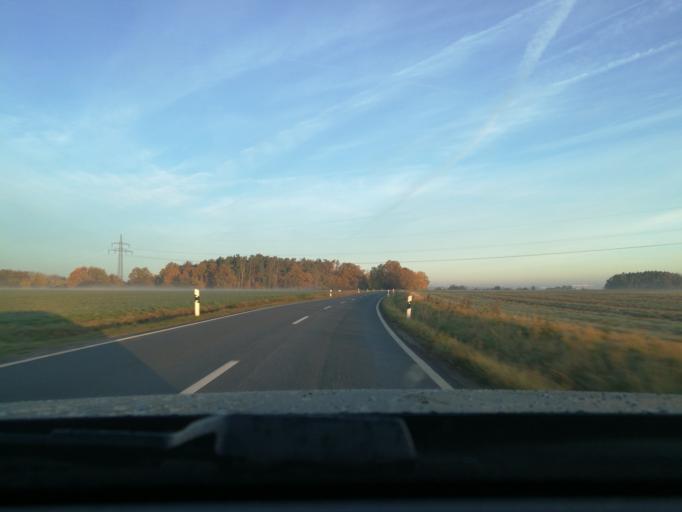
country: DE
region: Bavaria
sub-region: Regierungsbezirk Mittelfranken
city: Obermichelbach
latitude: 49.5513
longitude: 10.9240
